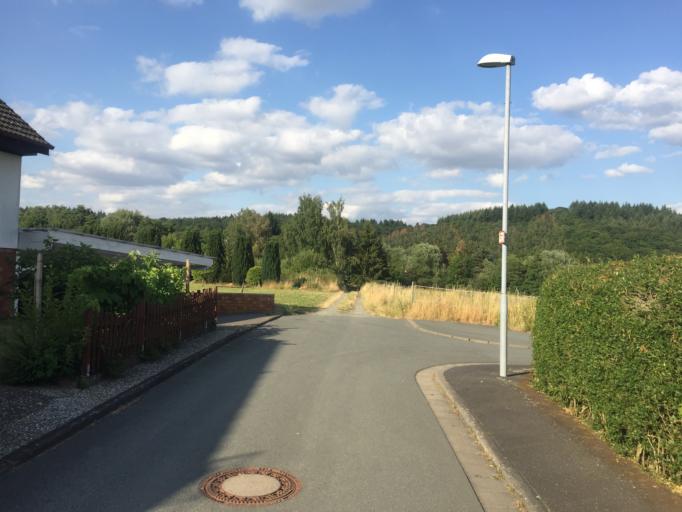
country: DE
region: Hesse
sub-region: Regierungsbezirk Giessen
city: Heuchelheim
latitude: 50.6431
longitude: 8.6006
